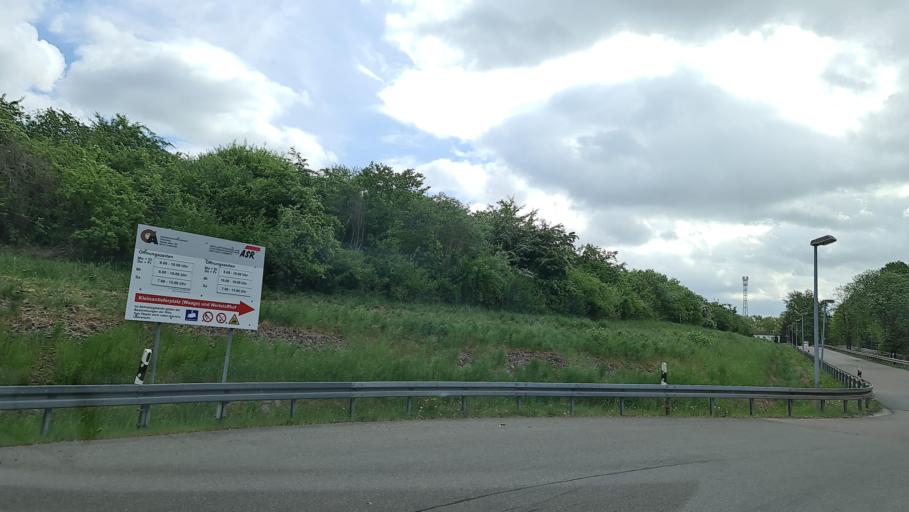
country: DE
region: Saxony
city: Hilbersdorf
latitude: 50.8514
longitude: 12.9758
